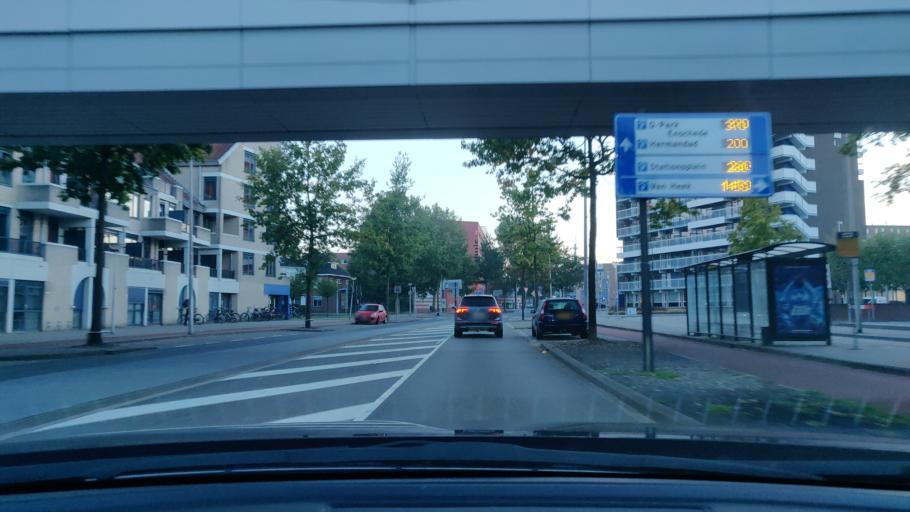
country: NL
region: Overijssel
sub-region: Gemeente Enschede
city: Enschede
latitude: 52.2169
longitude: 6.8899
